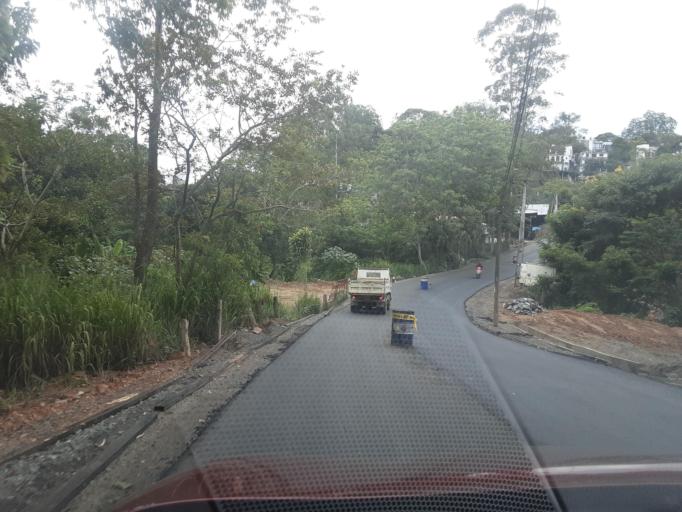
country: LK
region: Uva
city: Haputale
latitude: 6.8387
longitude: 81.0019
